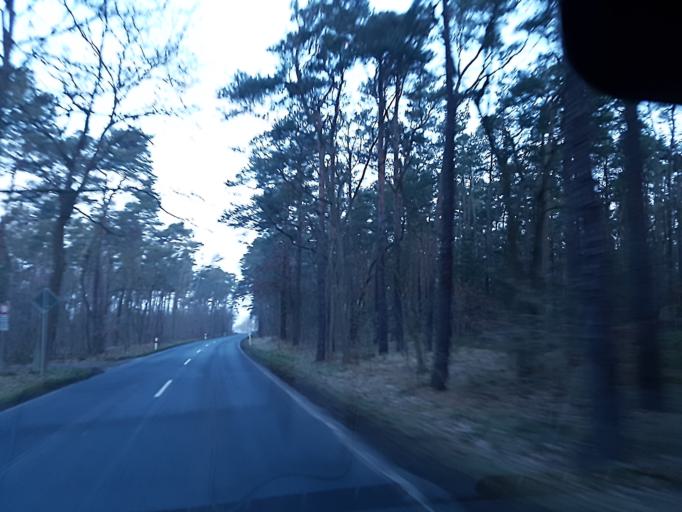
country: DE
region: Saxony-Anhalt
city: Holzdorf
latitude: 51.7764
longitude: 13.0780
